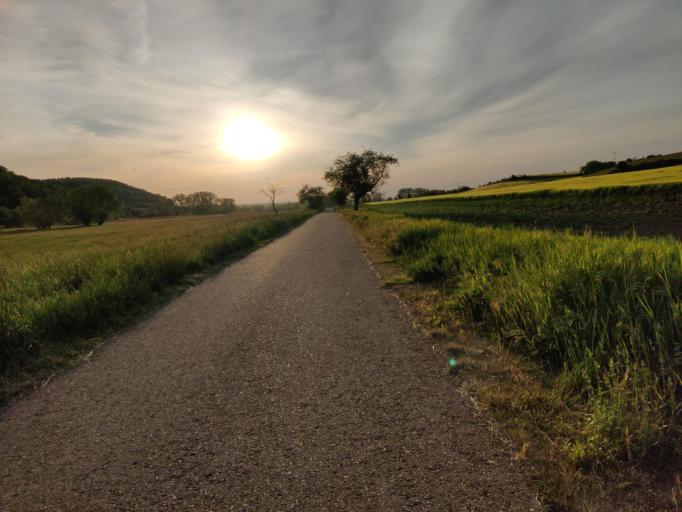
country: DE
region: Saxony-Anhalt
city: Balgstadt
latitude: 51.2136
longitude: 11.7155
